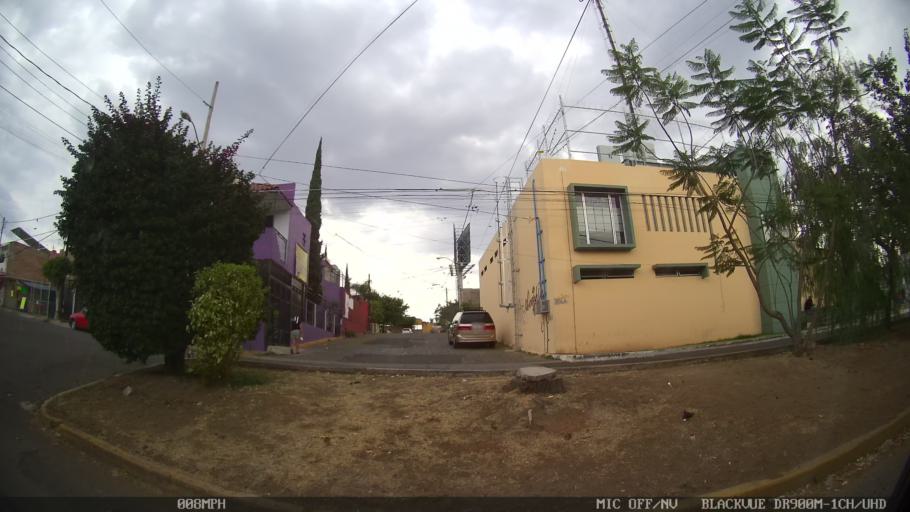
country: MX
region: Jalisco
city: Tlaquepaque
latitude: 20.6252
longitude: -103.2814
